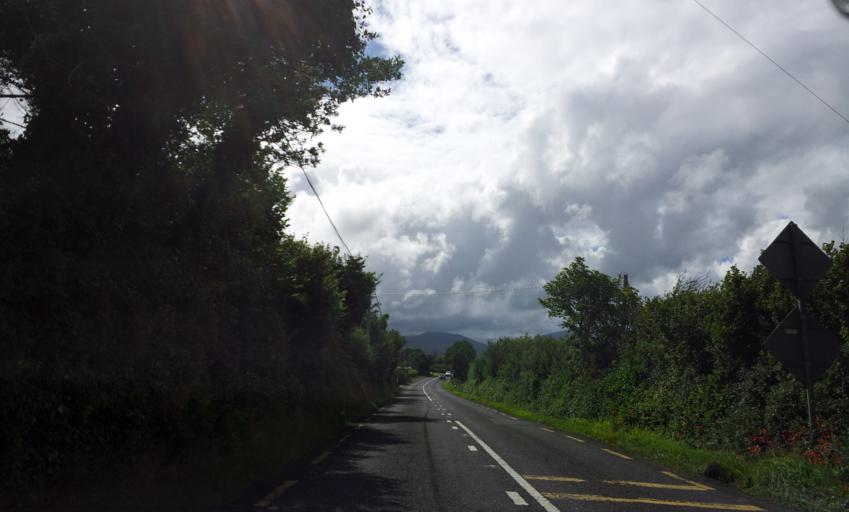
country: IE
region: Munster
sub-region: Ciarrai
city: Killorglin
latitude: 52.2296
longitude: -9.8757
